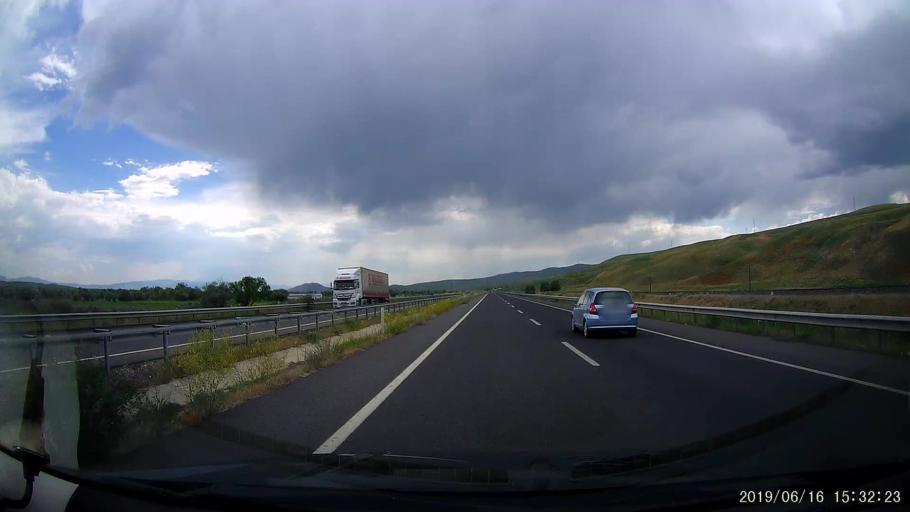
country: TR
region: Erzurum
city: Horasan
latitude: 40.0299
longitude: 42.0489
